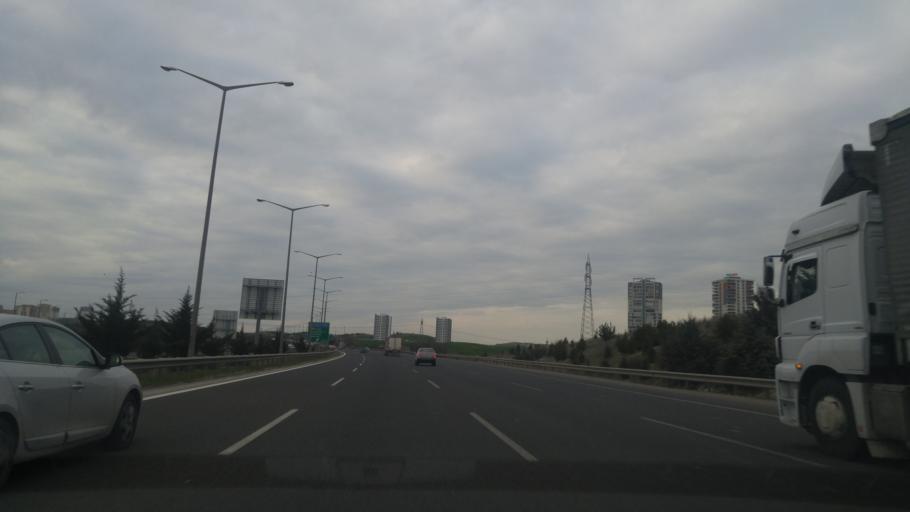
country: TR
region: Ankara
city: Etimesgut
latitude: 40.0003
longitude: 32.6363
